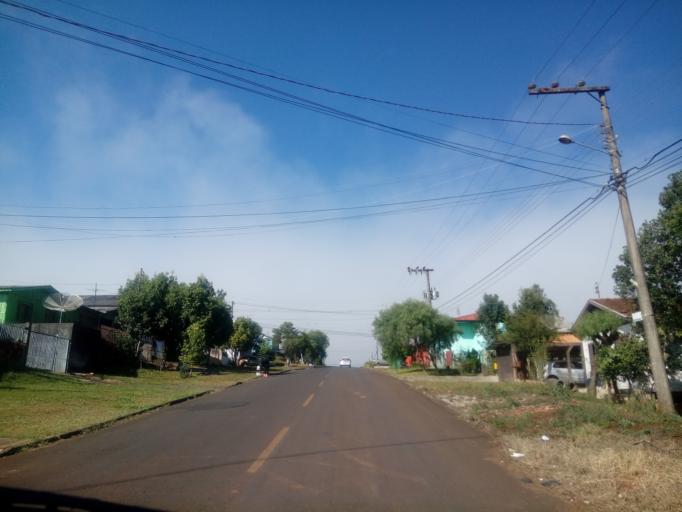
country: BR
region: Santa Catarina
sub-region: Chapeco
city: Chapeco
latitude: -27.0810
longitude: -52.6100
